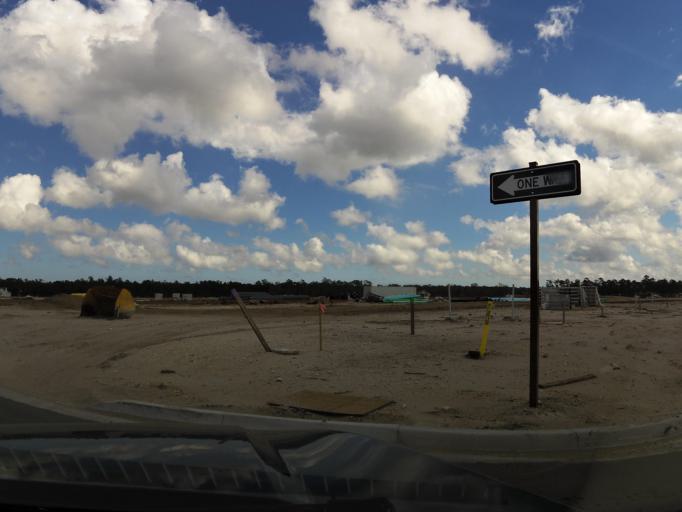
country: US
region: Florida
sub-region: Saint Johns County
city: Ponte Vedra Beach
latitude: 30.2451
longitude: -81.4954
